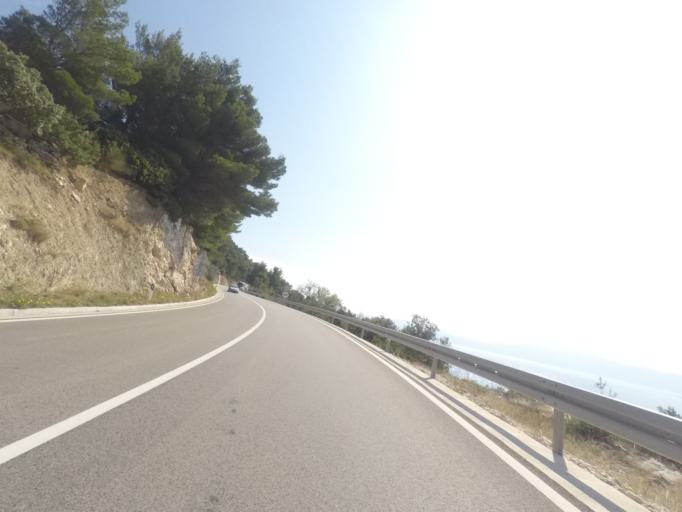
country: HR
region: Splitsko-Dalmatinska
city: Vrgorac
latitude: 43.1566
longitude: 17.2492
